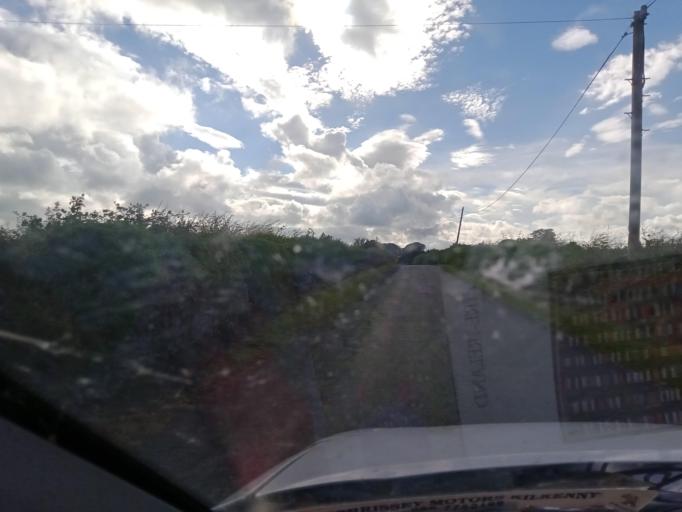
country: IE
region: Leinster
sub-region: Laois
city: Rathdowney
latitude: 52.7748
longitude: -7.5231
